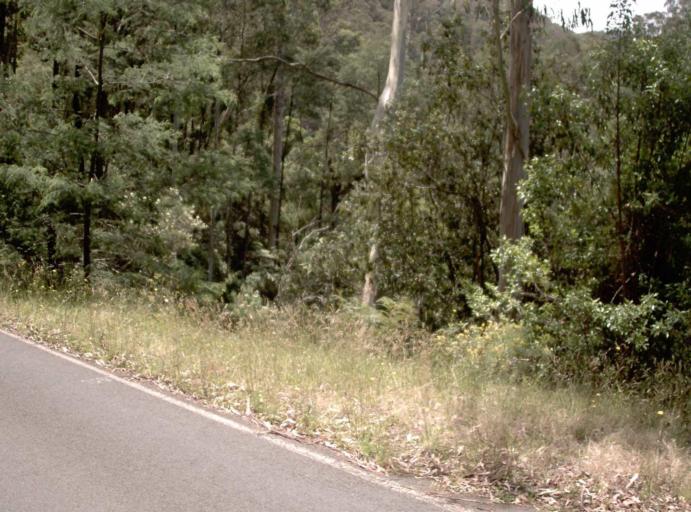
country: AU
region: Victoria
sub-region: Latrobe
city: Traralgon
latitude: -37.9546
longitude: 146.4243
